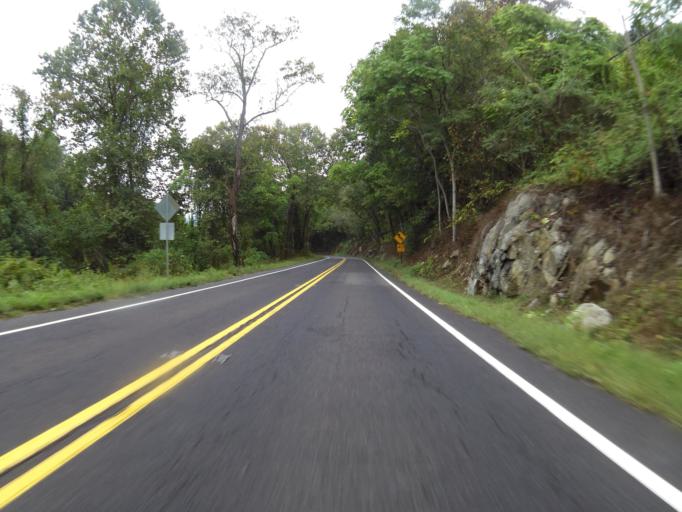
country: US
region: Virginia
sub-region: Rappahannock County
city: Washington
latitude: 38.6549
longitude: -78.2422
